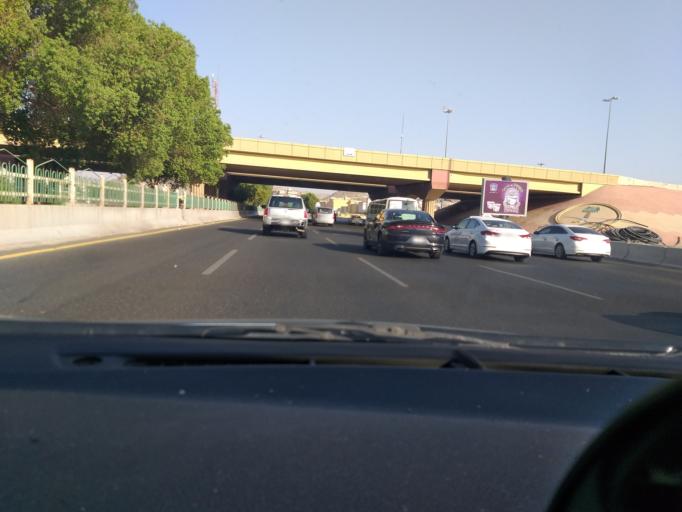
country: SA
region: Makkah
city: Mecca
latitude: 21.3674
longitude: 39.8870
